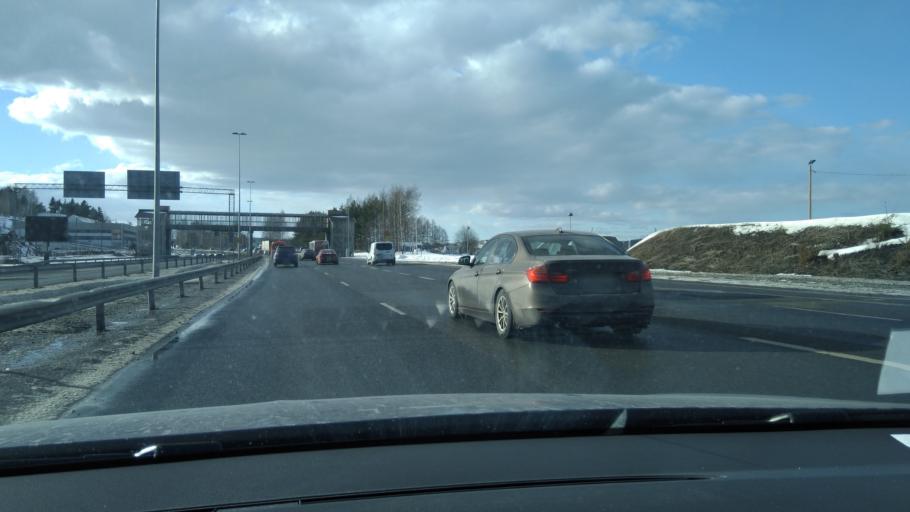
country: FI
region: Pirkanmaa
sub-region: Tampere
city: Tampere
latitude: 61.5054
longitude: 23.7176
